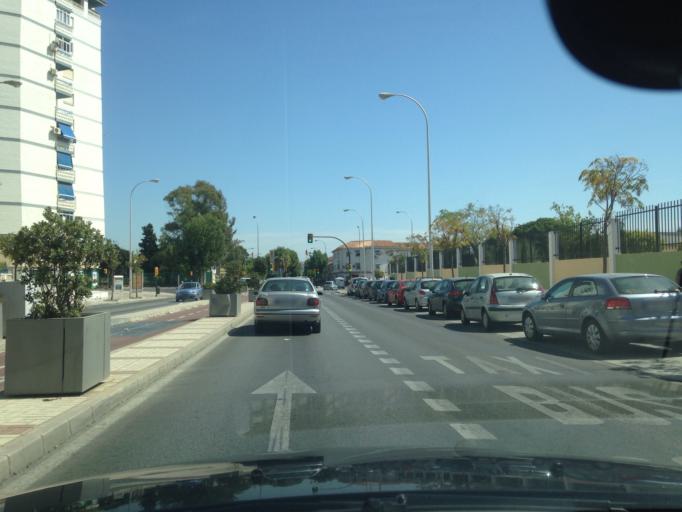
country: ES
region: Andalusia
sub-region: Provincia de Malaga
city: Malaga
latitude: 36.7191
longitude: -4.4504
